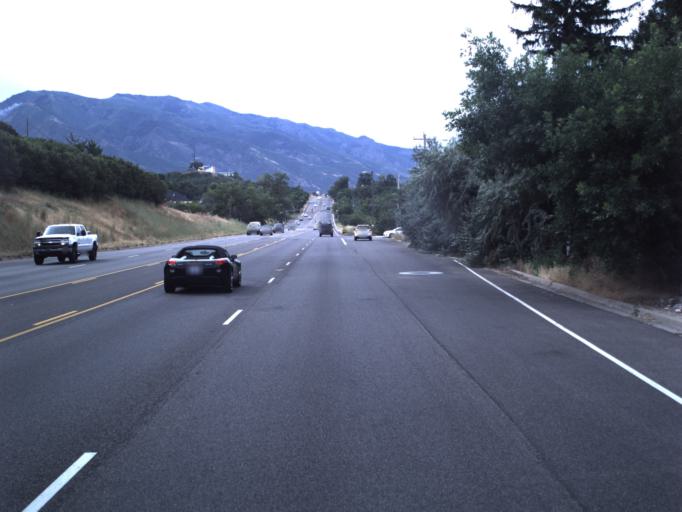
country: US
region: Utah
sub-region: Weber County
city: Washington Terrace
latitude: 41.1713
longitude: -111.9477
